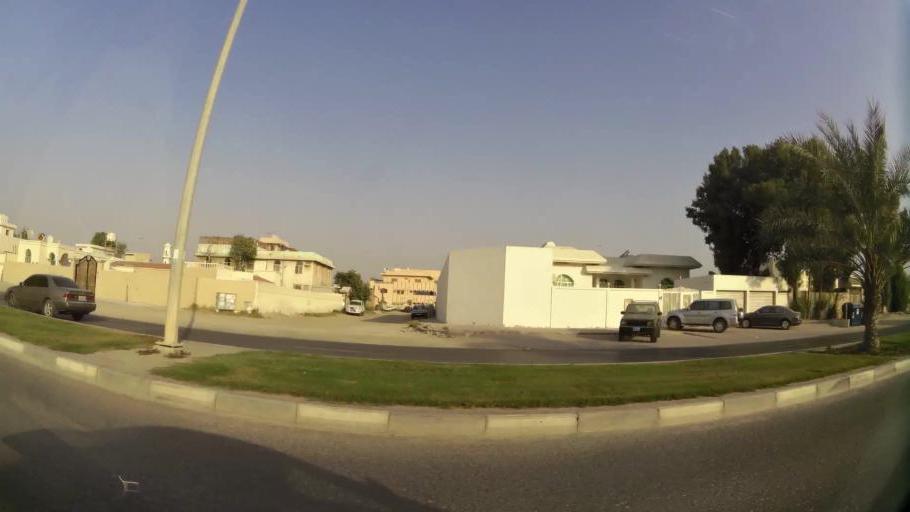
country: AE
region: Ajman
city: Ajman
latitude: 25.3796
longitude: 55.4364
